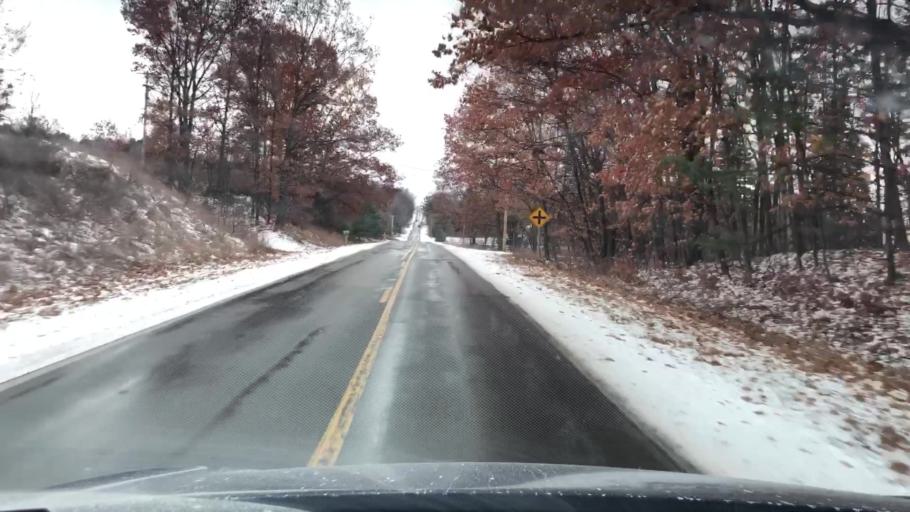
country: US
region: Michigan
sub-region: Antrim County
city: Elk Rapids
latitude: 44.8952
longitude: -85.5155
